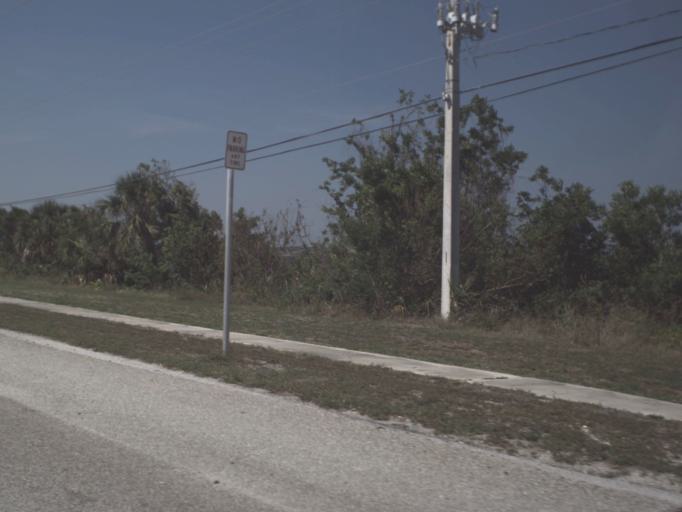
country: US
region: Florida
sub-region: Brevard County
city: South Patrick Shores
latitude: 28.1954
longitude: -80.6584
